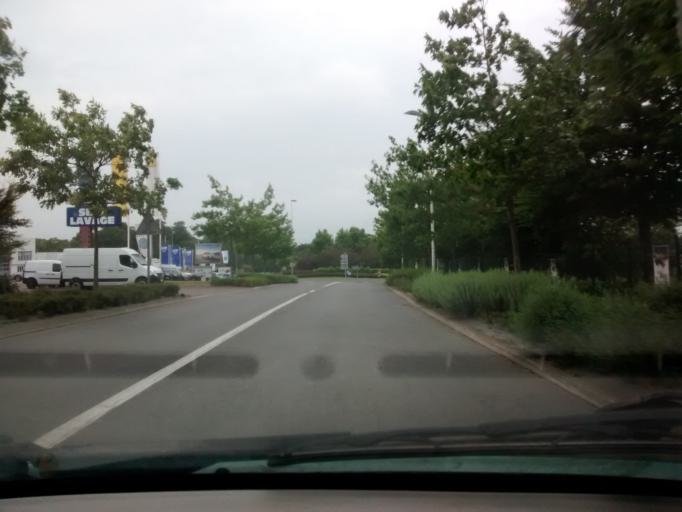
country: FR
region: Lower Normandy
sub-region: Departement de la Manche
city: Saint-Lo
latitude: 49.1049
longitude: -1.0671
